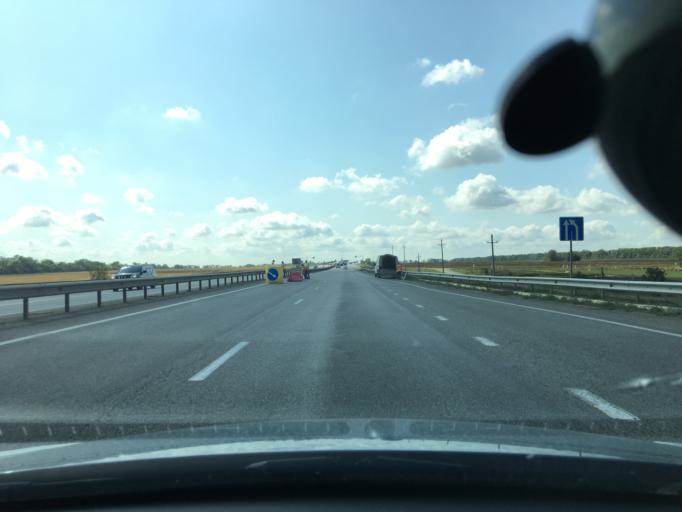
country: RU
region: Krasnodarskiy
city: Krasnoye
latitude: 46.7694
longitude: 39.6628
